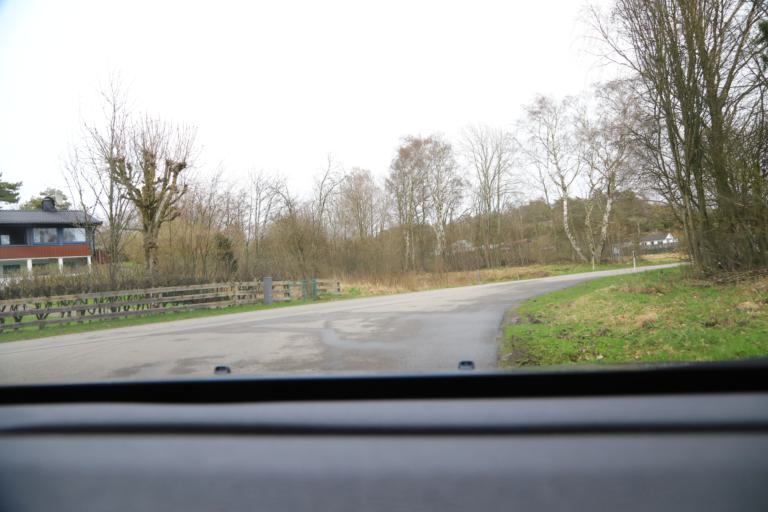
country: SE
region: Halland
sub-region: Kungsbacka Kommun
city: Frillesas
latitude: 57.2989
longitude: 12.1725
